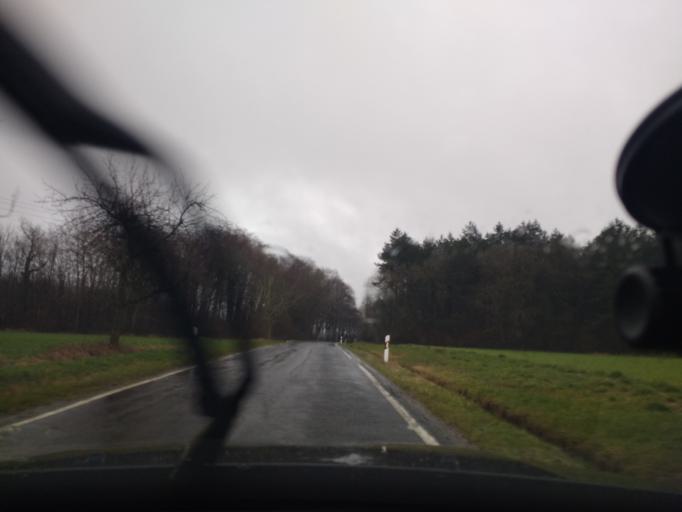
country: DE
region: Rheinland-Pfalz
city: Onsdorf
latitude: 49.6512
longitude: 6.4698
